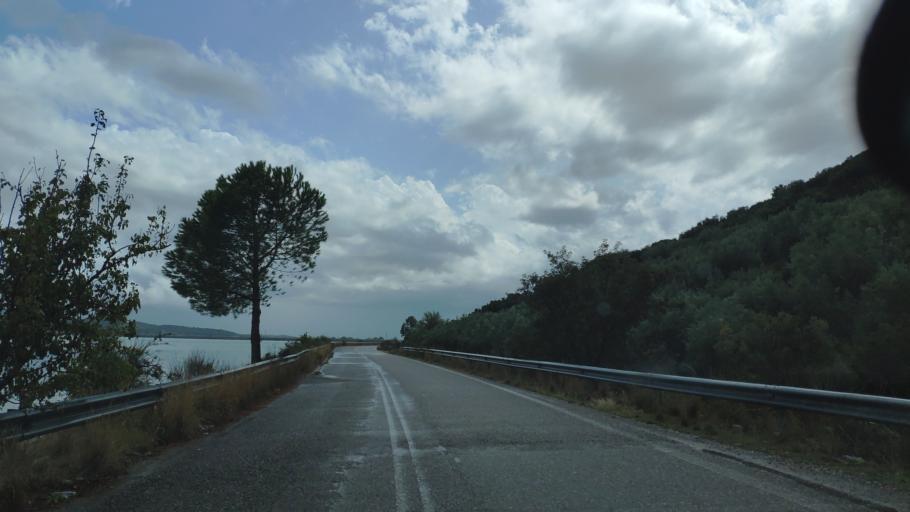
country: GR
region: West Greece
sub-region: Nomos Aitolias kai Akarnanias
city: Lepenou
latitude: 38.6894
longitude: 21.3215
